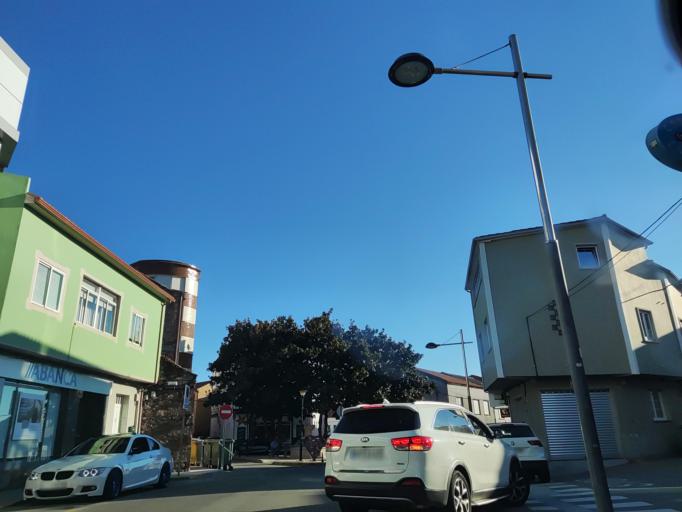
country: ES
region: Galicia
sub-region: Provincia da Coruna
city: Boiro
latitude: 42.6173
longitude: -8.8835
